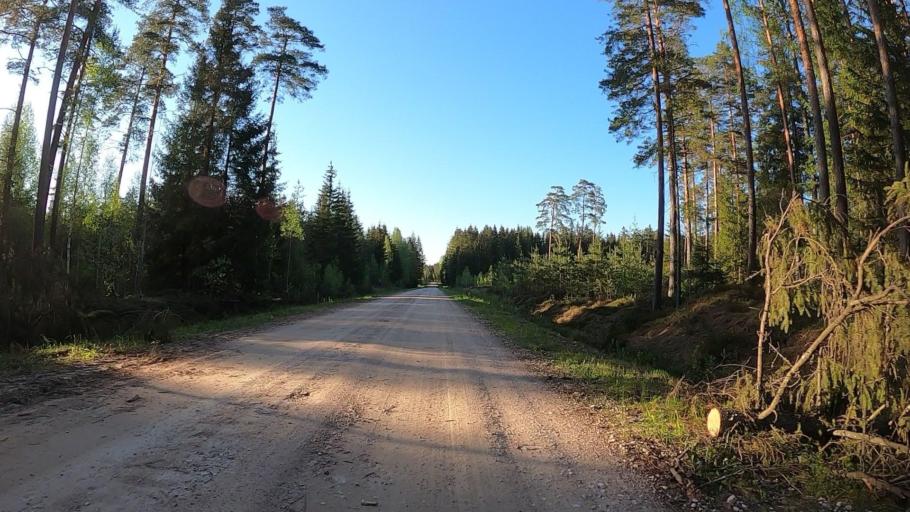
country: LV
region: Kekava
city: Kekava
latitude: 56.7509
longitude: 24.2310
